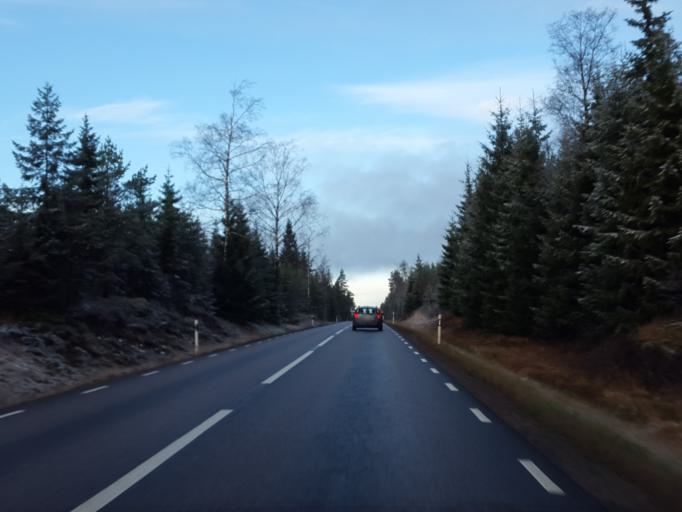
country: SE
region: Vaestra Goetaland
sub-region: Boras Kommun
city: Sjomarken
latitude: 57.7562
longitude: 12.8524
